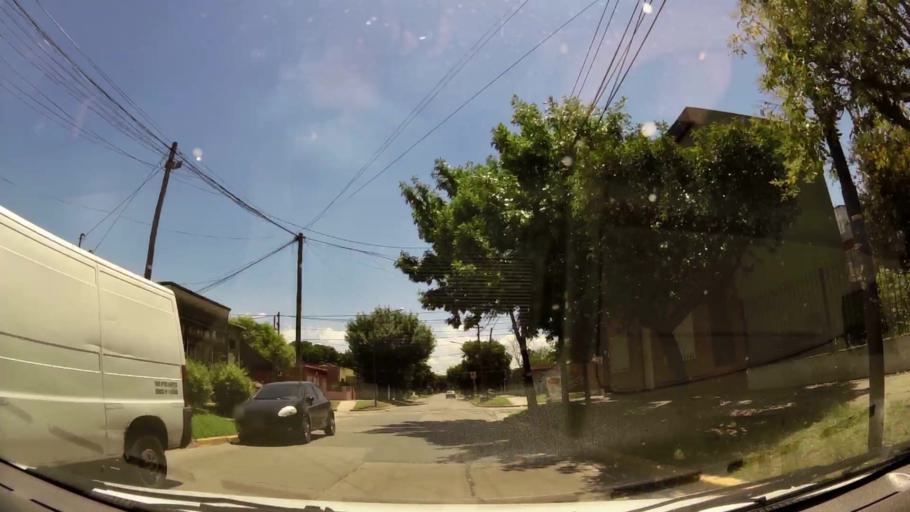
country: AR
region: Buenos Aires
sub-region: Partido de Merlo
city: Merlo
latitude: -34.6585
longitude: -58.7129
